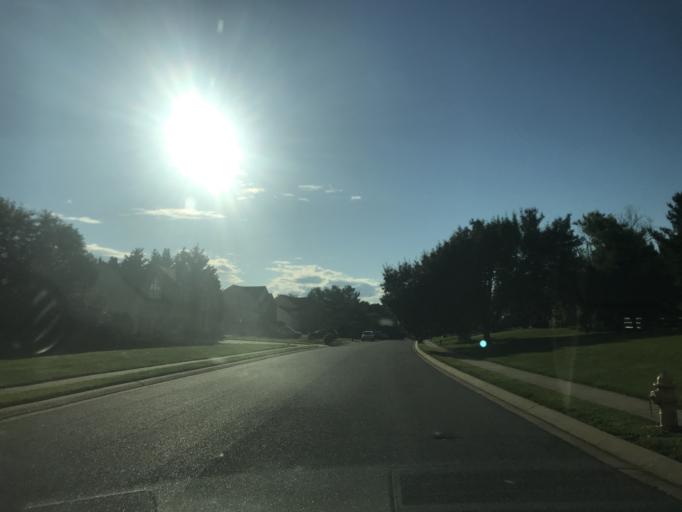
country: US
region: Maryland
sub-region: Harford County
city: South Bel Air
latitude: 39.5624
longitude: -76.3185
